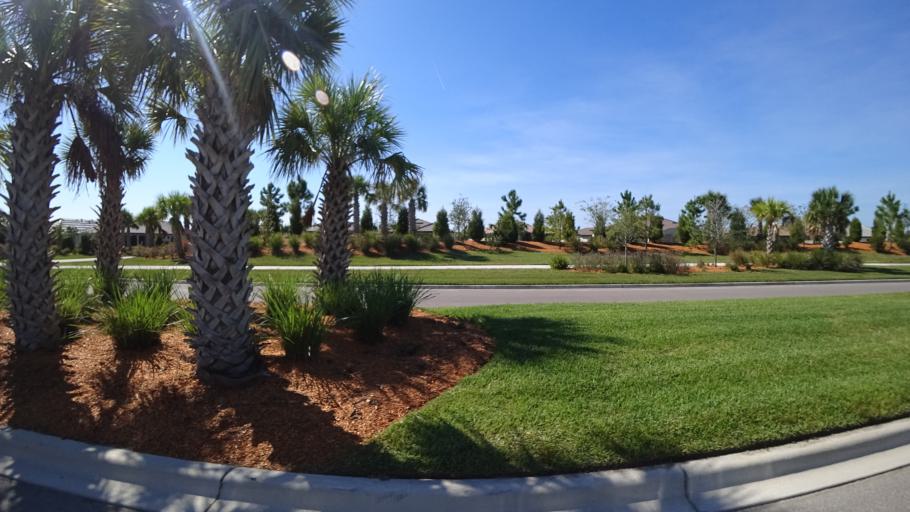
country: US
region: Florida
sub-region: Sarasota County
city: The Meadows
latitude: 27.4092
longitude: -82.3614
